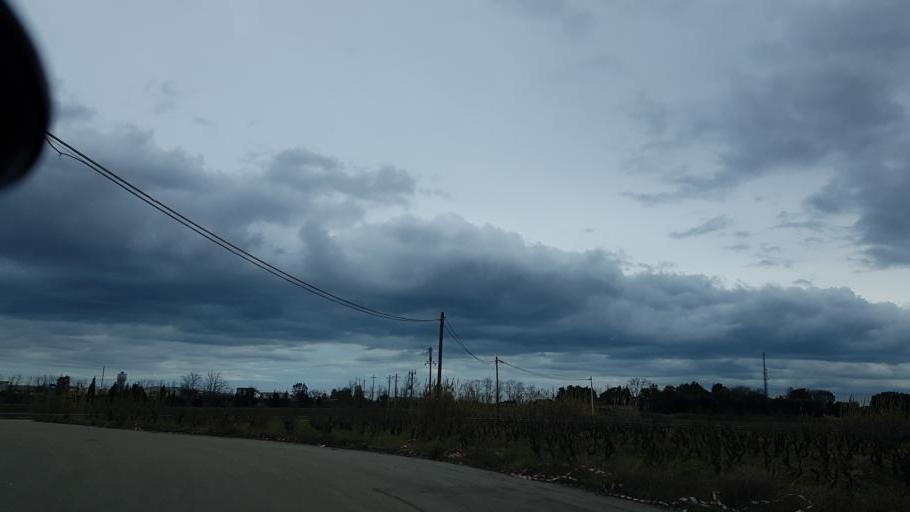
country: IT
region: Apulia
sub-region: Provincia di Brindisi
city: La Rosa
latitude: 40.6131
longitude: 17.9499
